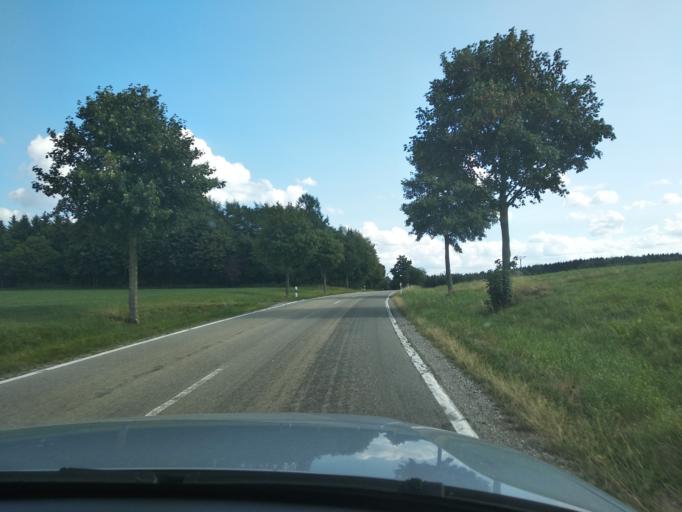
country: DE
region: Baden-Wuerttemberg
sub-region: Tuebingen Region
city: Leutkirch im Allgau
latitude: 47.8830
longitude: 9.9845
